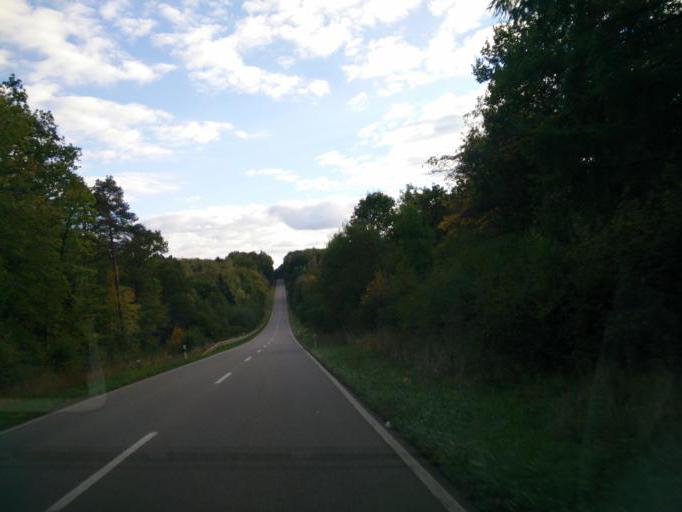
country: DE
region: Baden-Wuerttemberg
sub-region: Tuebingen Region
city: Dettenhausen
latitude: 48.5831
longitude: 9.1055
